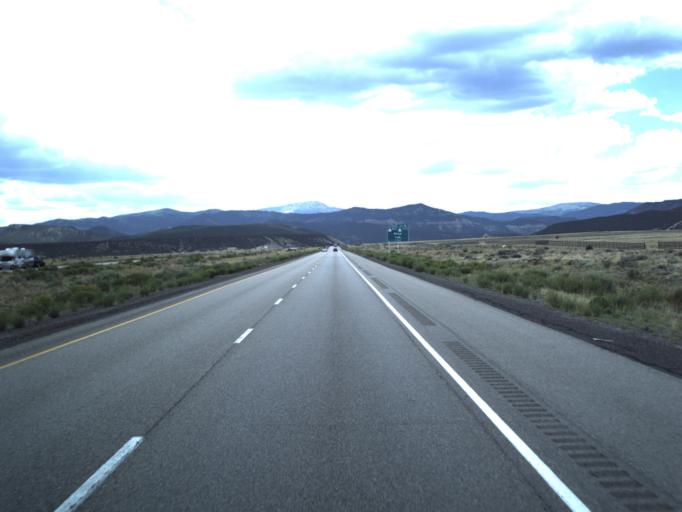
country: US
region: Utah
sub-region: Emery County
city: Ferron
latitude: 38.7758
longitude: -111.3232
